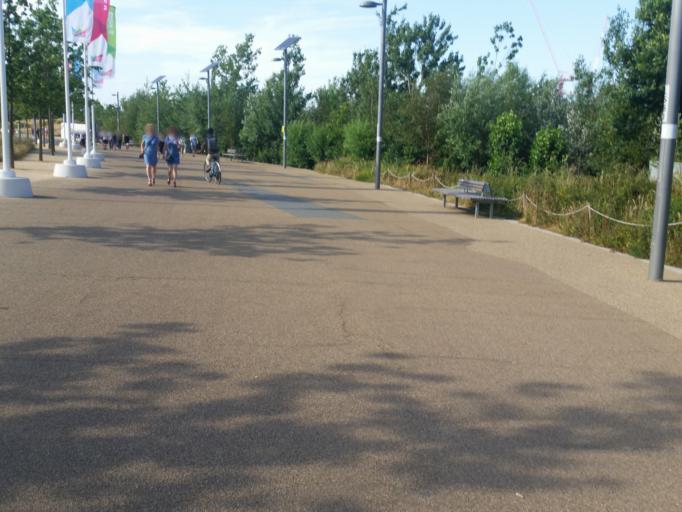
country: GB
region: England
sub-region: Greater London
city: Hackney
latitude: 51.5446
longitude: -0.0175
